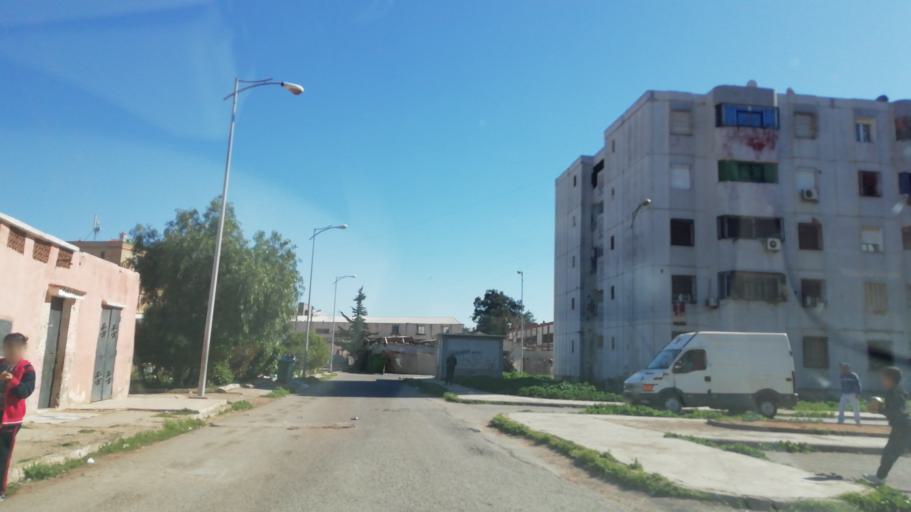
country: DZ
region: Oran
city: Oran
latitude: 35.6886
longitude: -0.6101
